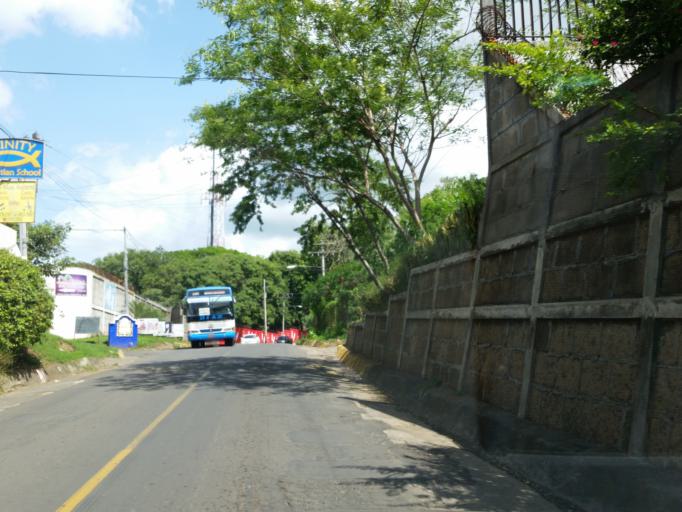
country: NI
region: Managua
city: Managua
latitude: 12.0942
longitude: -86.2467
